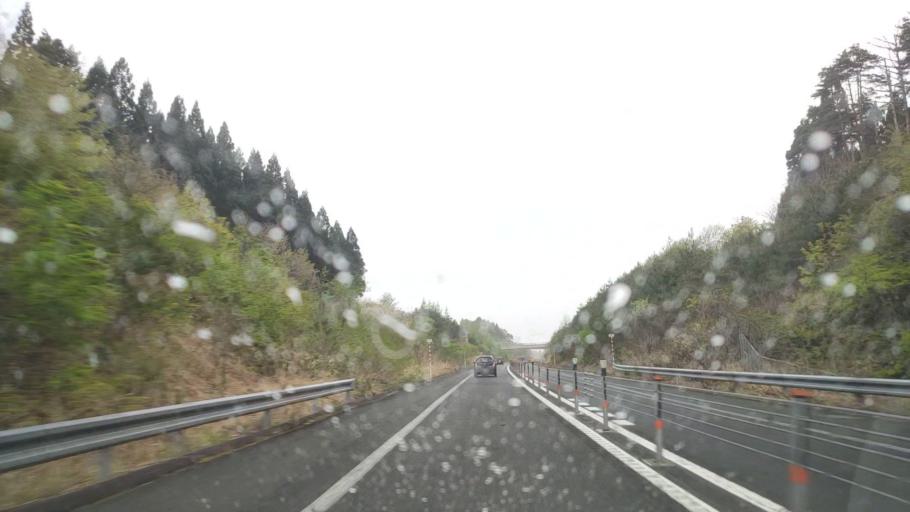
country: JP
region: Akita
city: Noshiromachi
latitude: 40.2035
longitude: 140.1580
